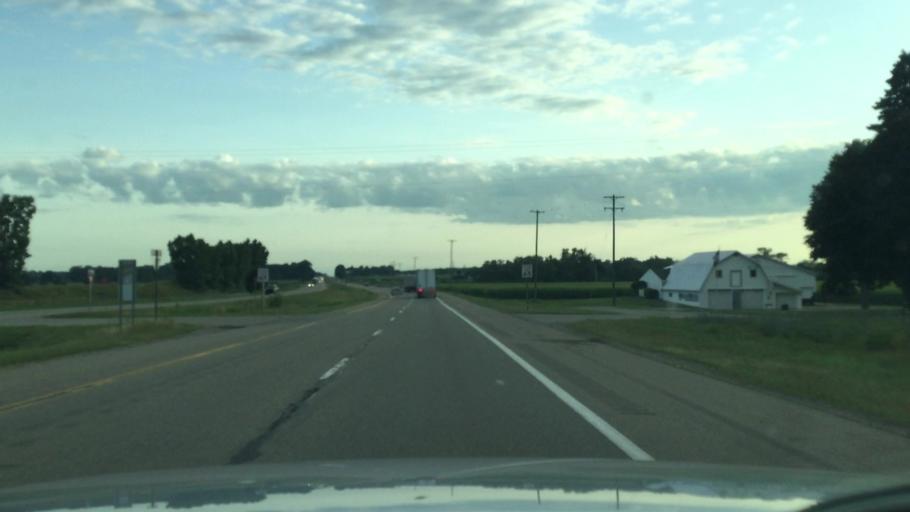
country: US
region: Michigan
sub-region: Clinton County
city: Saint Johns
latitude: 43.0417
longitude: -84.5638
